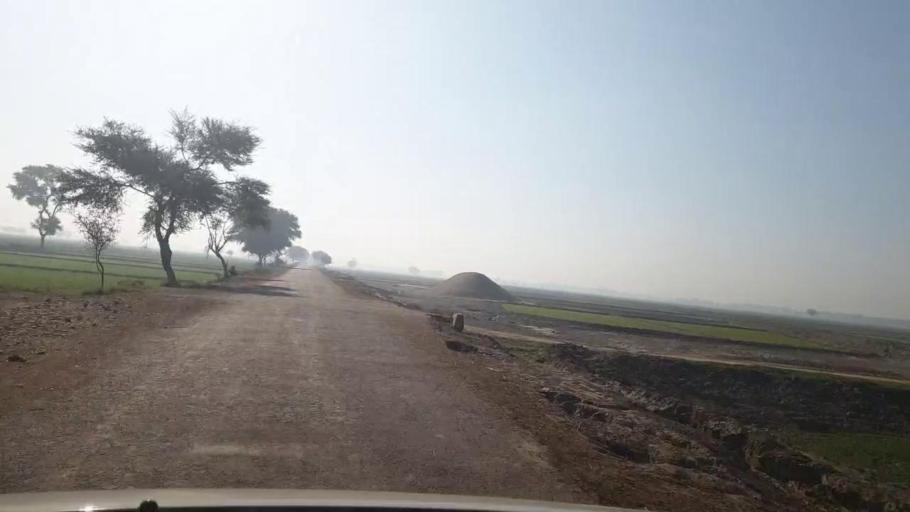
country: PK
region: Sindh
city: Dadu
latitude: 26.6712
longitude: 67.8143
